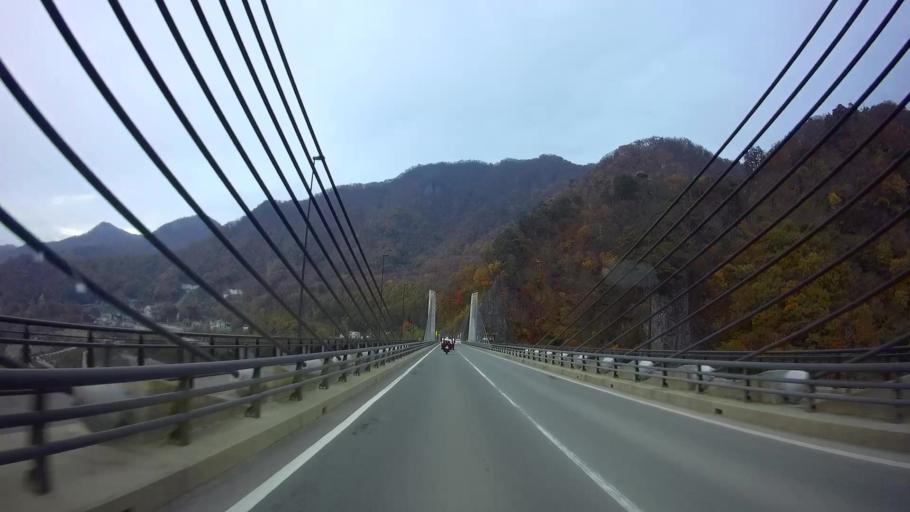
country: JP
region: Gunma
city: Nakanojomachi
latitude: 36.5450
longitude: 138.6881
